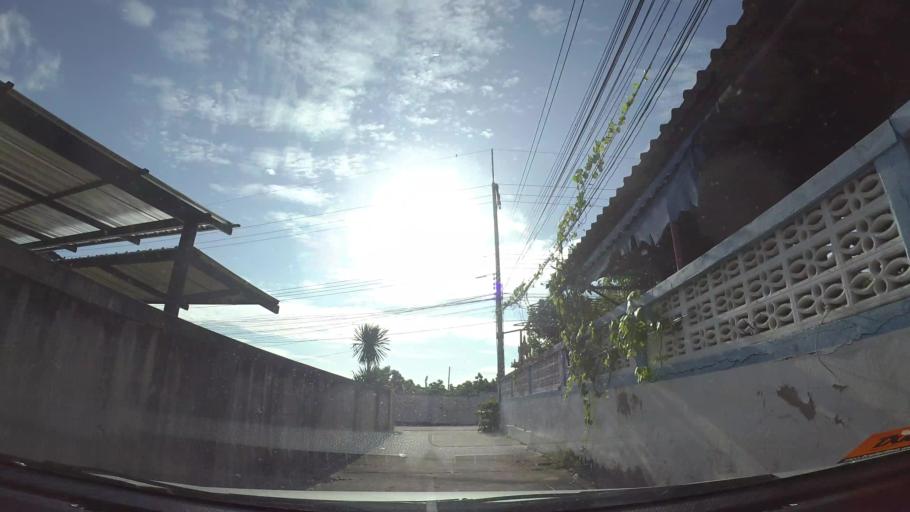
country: TH
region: Chon Buri
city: Sattahip
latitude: 12.6720
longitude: 100.9127
